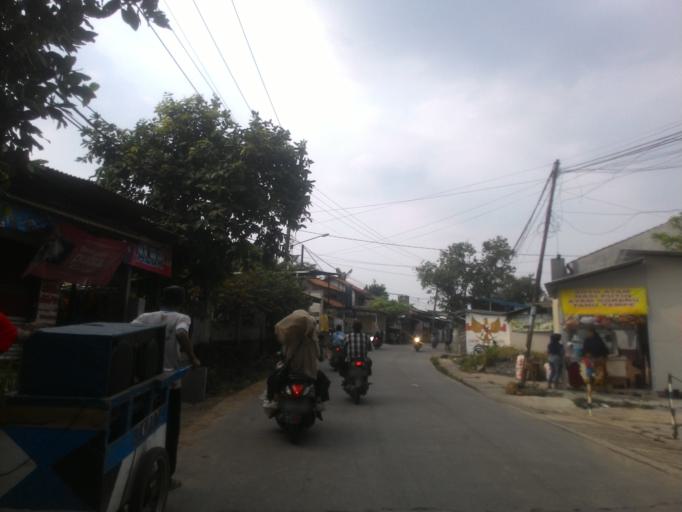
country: ID
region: West Java
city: Cibinong
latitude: -6.4574
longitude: 106.8393
